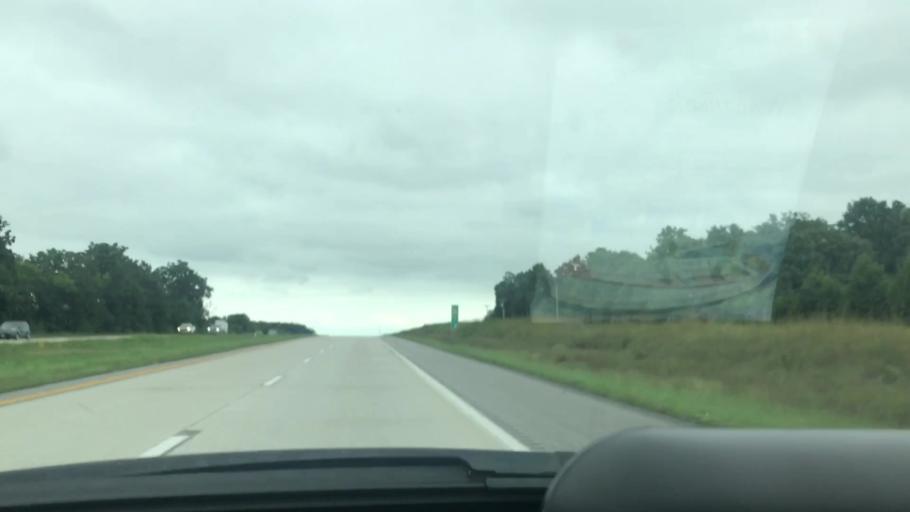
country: US
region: Missouri
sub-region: Greene County
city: Fair Grove
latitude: 37.4826
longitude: -93.1392
